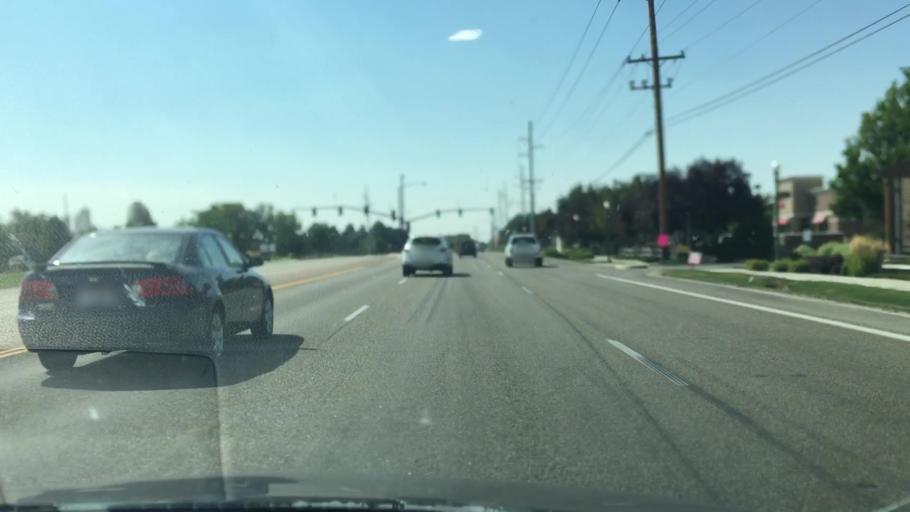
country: US
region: Idaho
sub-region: Ada County
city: Eagle
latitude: 43.6831
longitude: -116.3154
